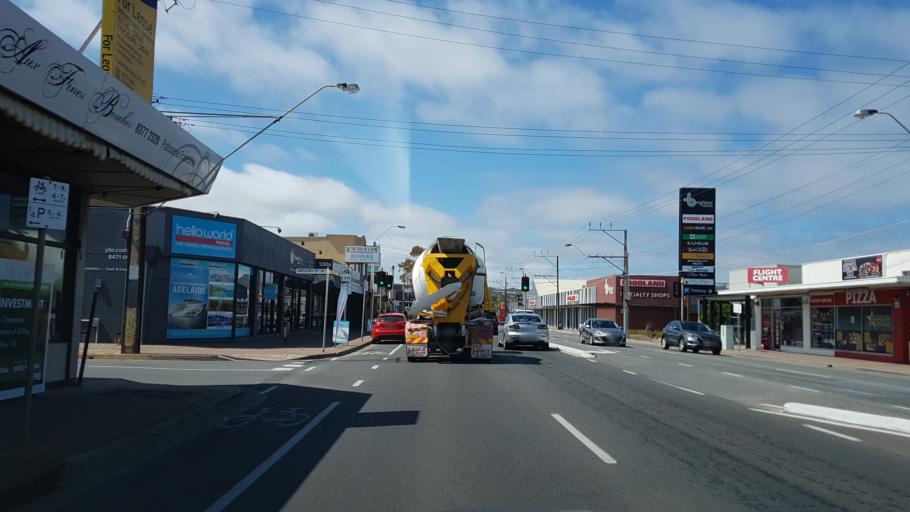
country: AU
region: South Australia
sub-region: Adelaide
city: Brighton
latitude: -35.0208
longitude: 138.5233
